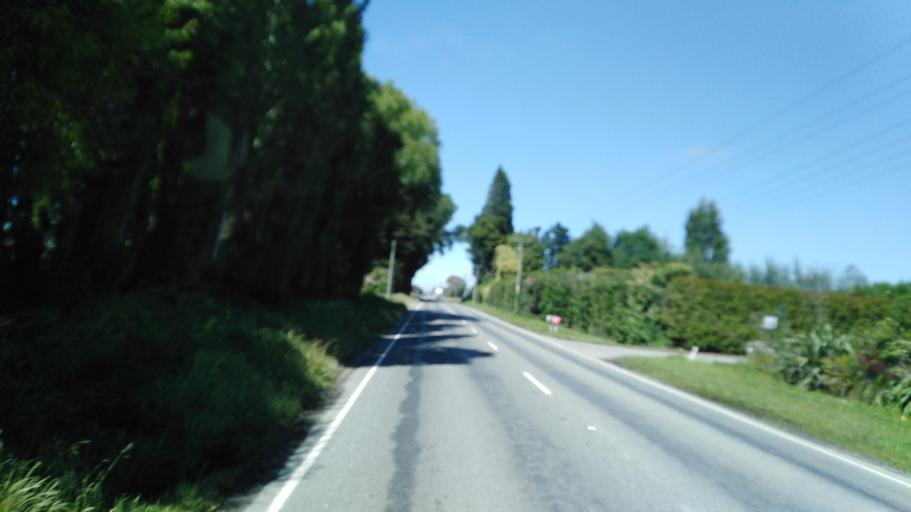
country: NZ
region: Canterbury
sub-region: Selwyn District
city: Prebbleton
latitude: -43.5233
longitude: 172.5026
